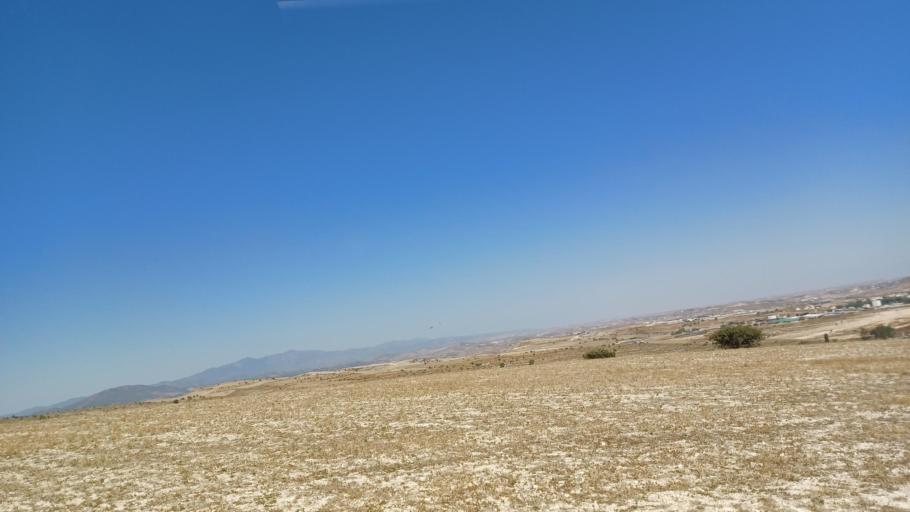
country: CY
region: Lefkosia
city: Lympia
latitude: 34.9807
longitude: 33.4848
